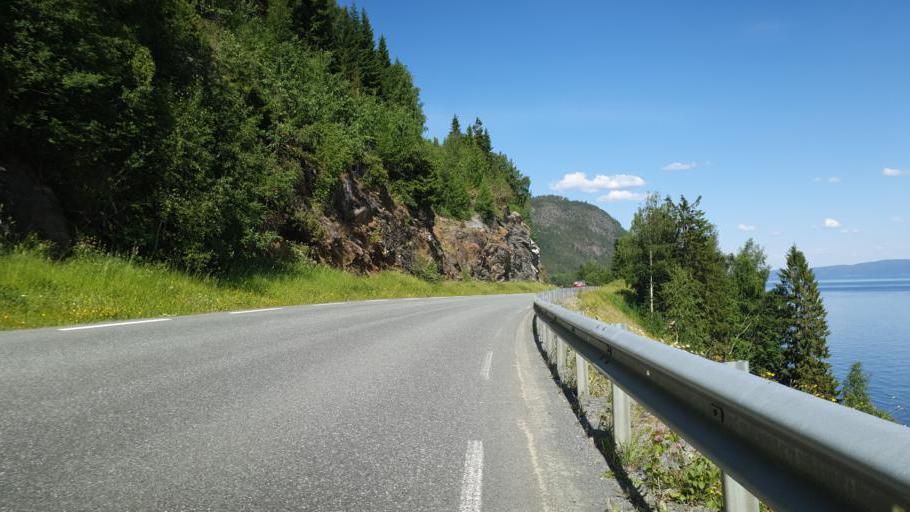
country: NO
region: Nord-Trondelag
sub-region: Leksvik
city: Leksvik
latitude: 63.6174
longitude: 10.5182
